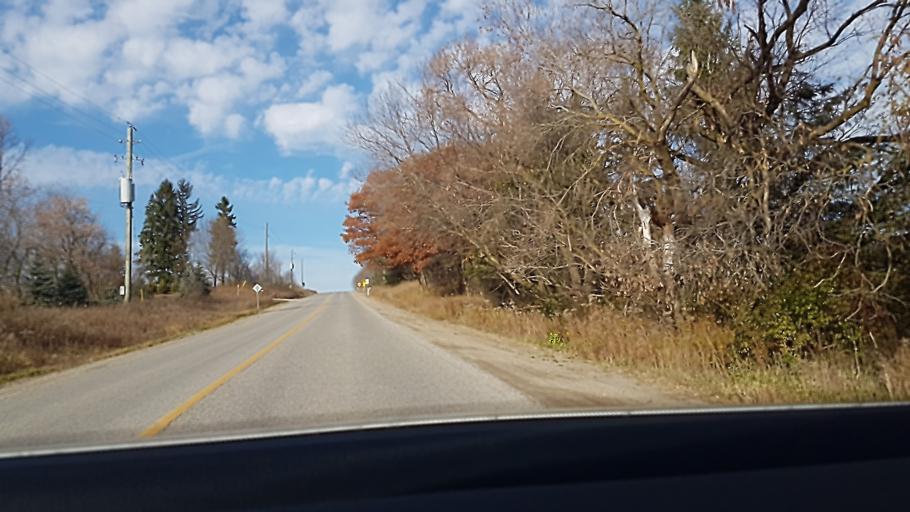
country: CA
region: Ontario
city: Bradford West Gwillimbury
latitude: 44.0517
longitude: -79.7740
